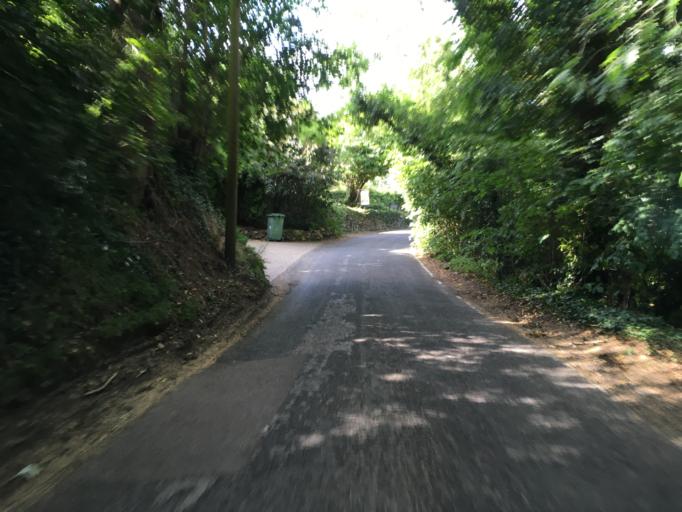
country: GB
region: England
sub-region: Kent
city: Maidstone
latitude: 51.2434
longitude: 0.5112
